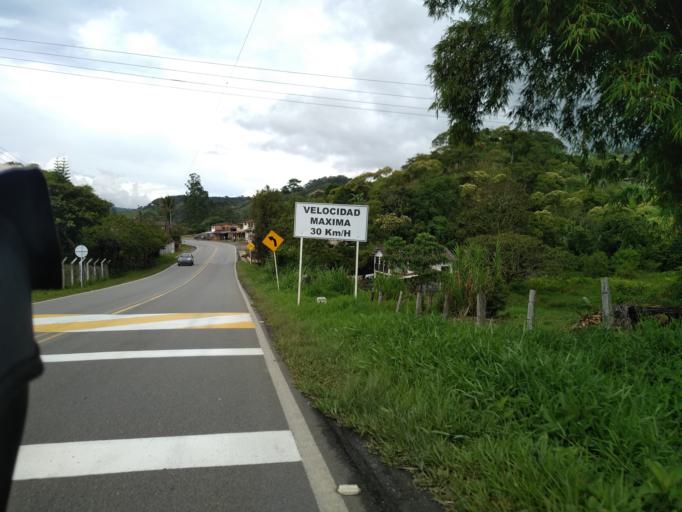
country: CO
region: Santander
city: Suaita
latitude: 6.1229
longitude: -73.3657
